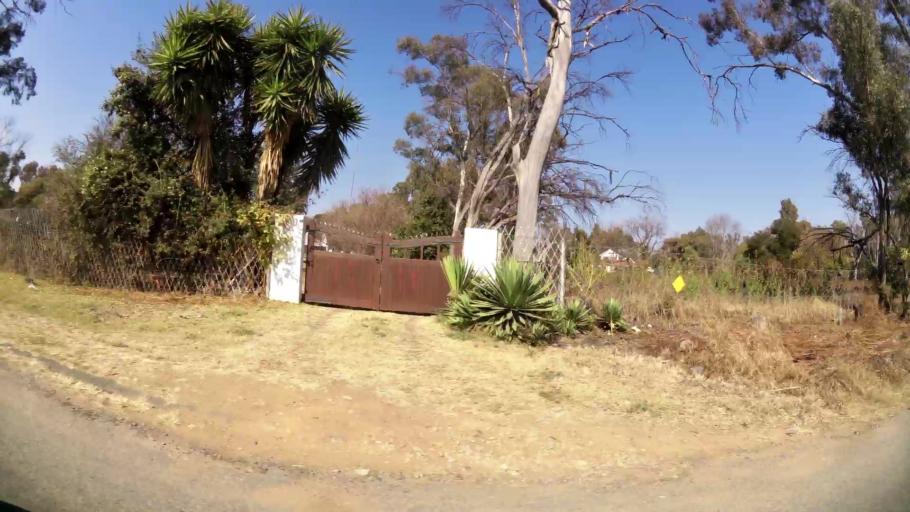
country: ZA
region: Gauteng
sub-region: City of Johannesburg Metropolitan Municipality
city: Modderfontein
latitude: -26.0943
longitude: 28.1336
